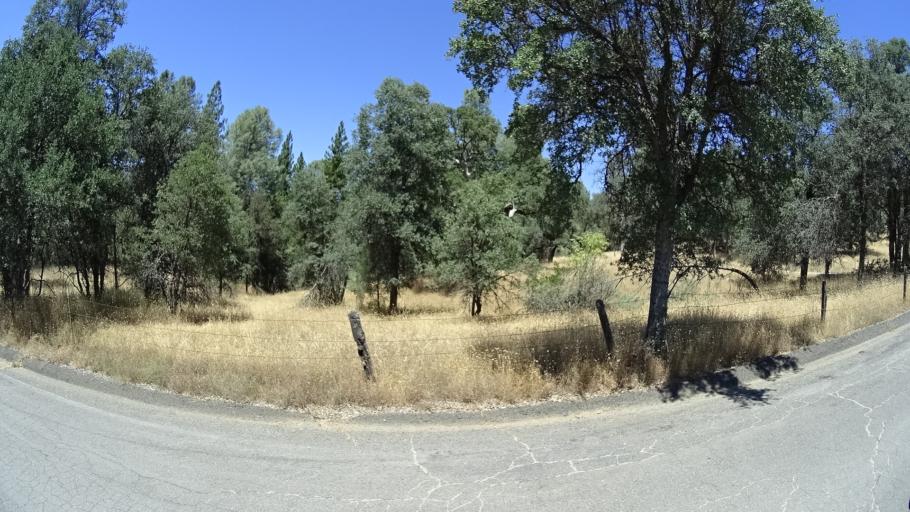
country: US
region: California
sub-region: Calaveras County
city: Mountain Ranch
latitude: 38.2651
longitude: -120.4740
